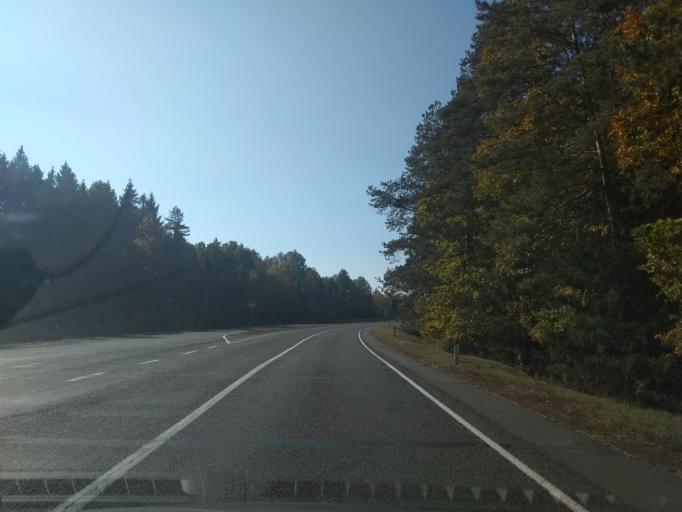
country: BY
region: Brest
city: Ivatsevichy
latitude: 52.8565
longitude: 25.6516
